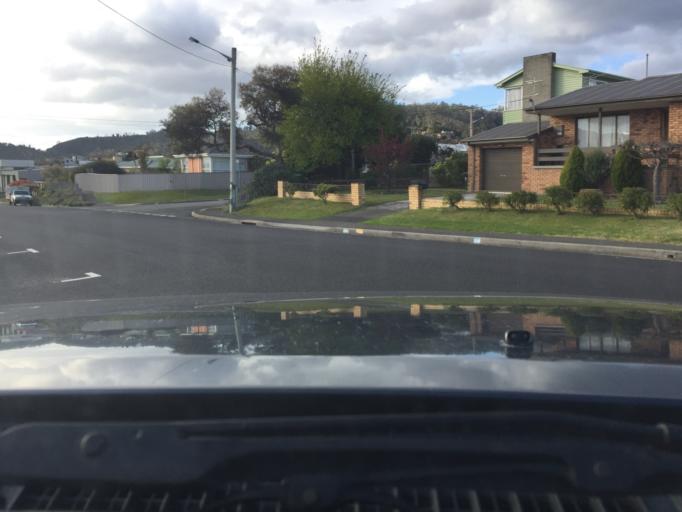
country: AU
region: Tasmania
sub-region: Clarence
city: Howrah
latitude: -42.8821
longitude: 147.4081
